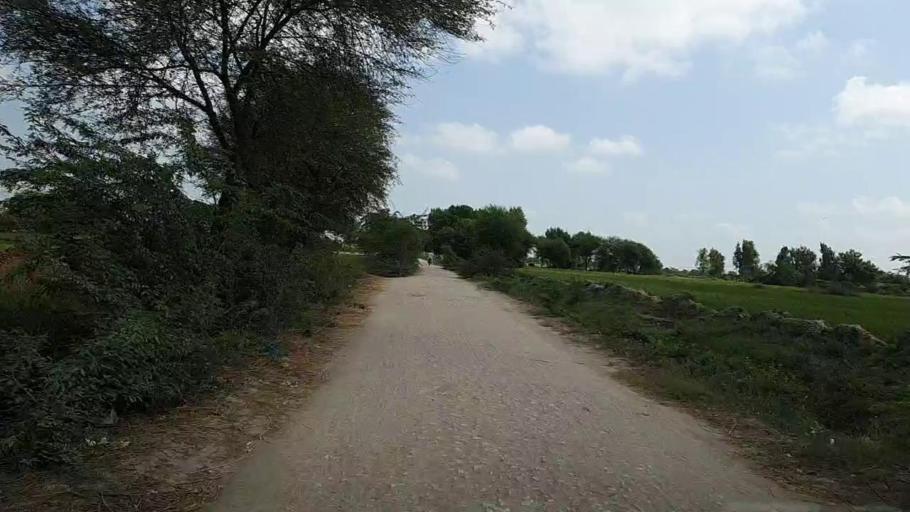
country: PK
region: Sindh
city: Kario
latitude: 24.6754
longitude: 68.5385
